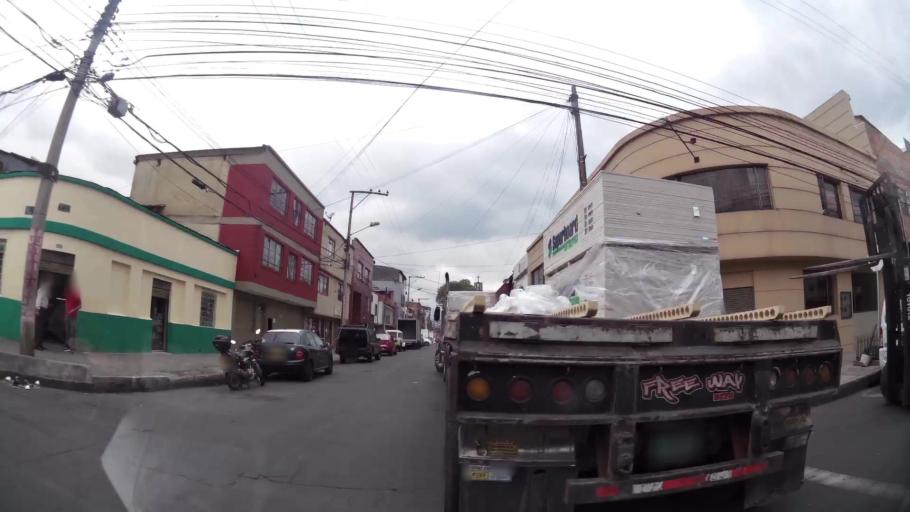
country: CO
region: Bogota D.C.
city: Barrio San Luis
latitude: 4.6697
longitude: -74.0681
